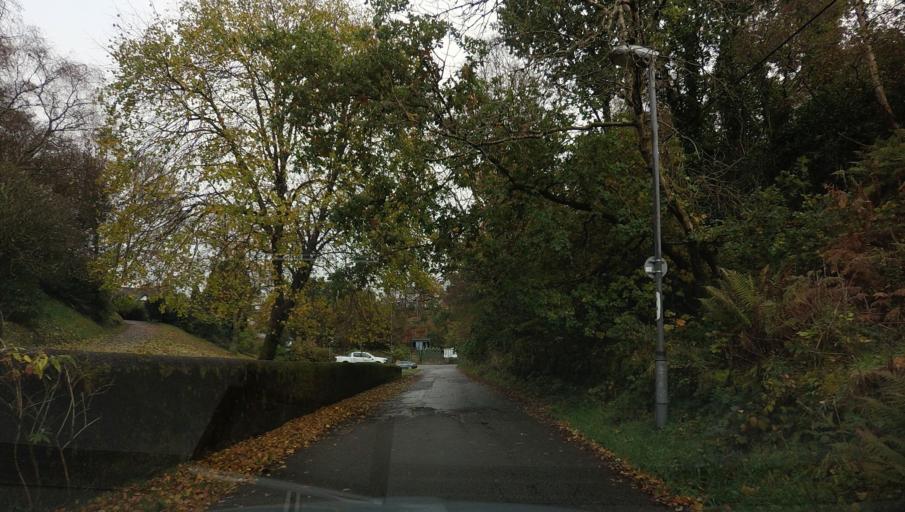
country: GB
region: Scotland
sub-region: Argyll and Bute
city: Oban
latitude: 56.4158
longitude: -5.4684
